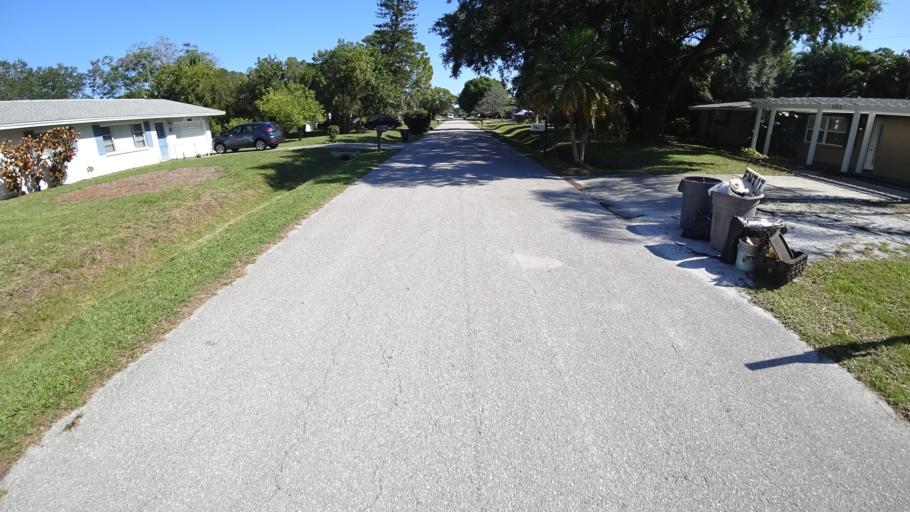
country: US
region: Florida
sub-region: Manatee County
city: West Bradenton
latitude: 27.4821
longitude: -82.6084
